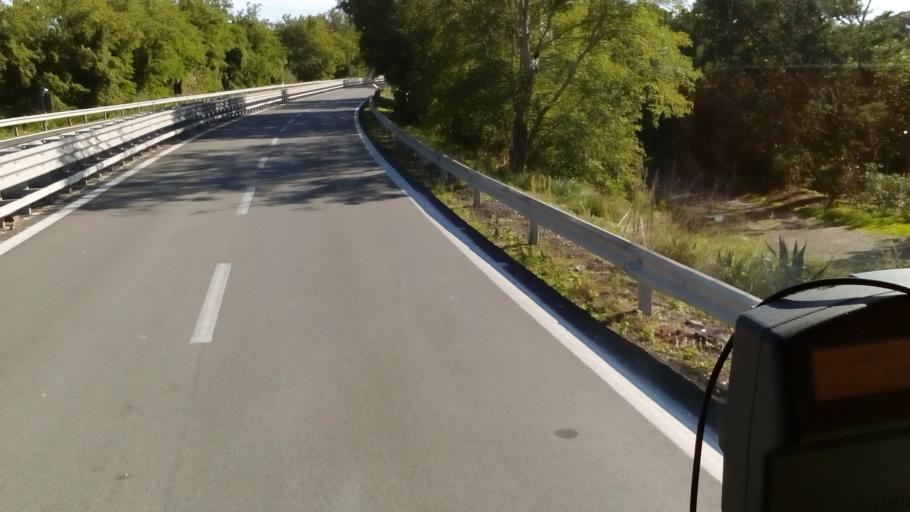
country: IT
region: Latium
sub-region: Provincia di Viterbo
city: Montalto di Castro
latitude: 42.3169
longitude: 11.6529
